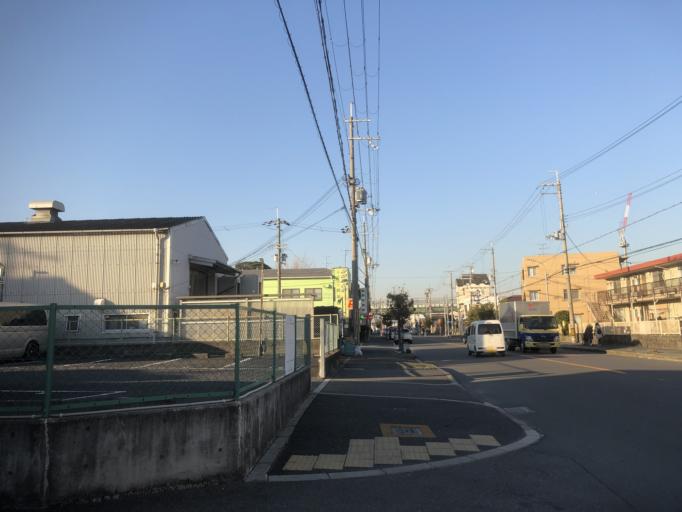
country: JP
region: Osaka
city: Daitocho
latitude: 34.6765
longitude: 135.5788
